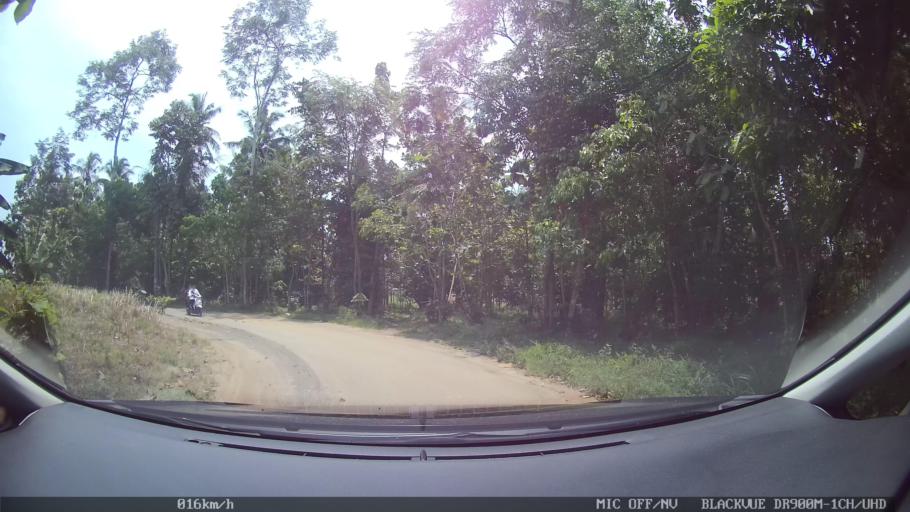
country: ID
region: Lampung
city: Natar
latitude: -5.3152
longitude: 105.2477
